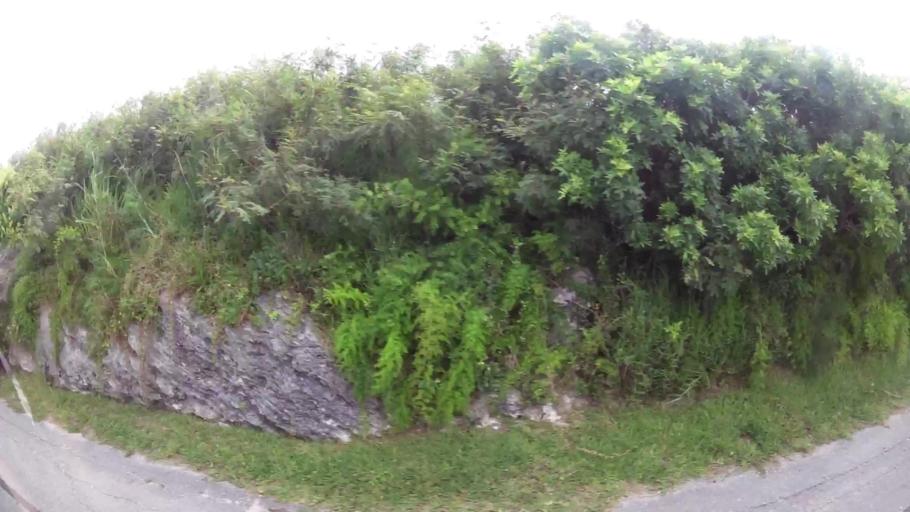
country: BM
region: Saint George
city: Saint George
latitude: 32.3871
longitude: -64.6781
